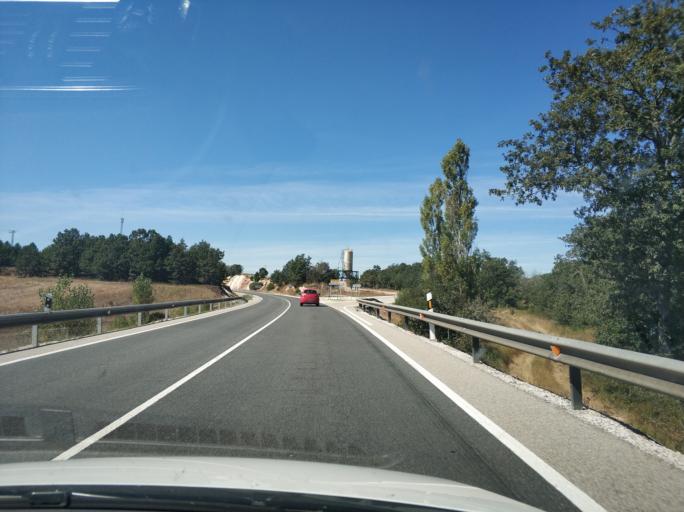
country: ES
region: Castille and Leon
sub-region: Provincia de Burgos
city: Basconcillos del Tozo
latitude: 42.7092
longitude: -4.0034
